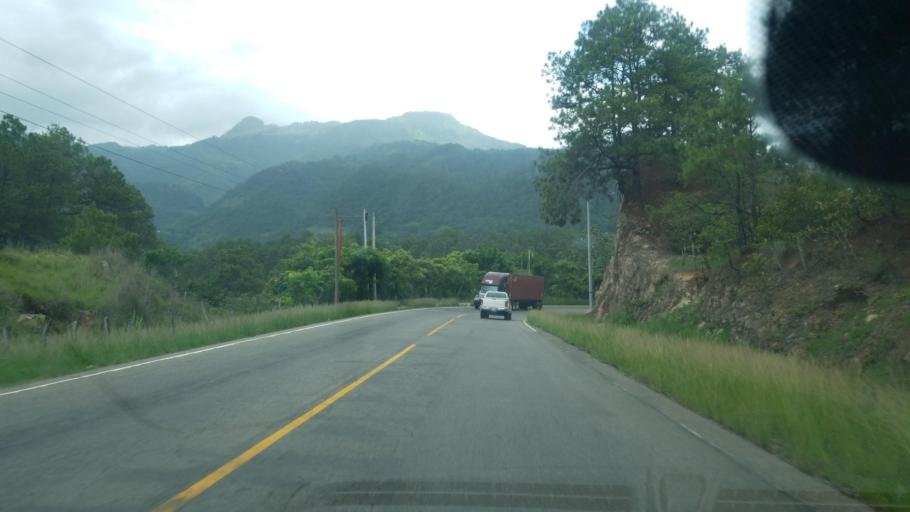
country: HN
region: Ocotepeque
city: Sinuapa
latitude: 14.4584
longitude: -89.1631
